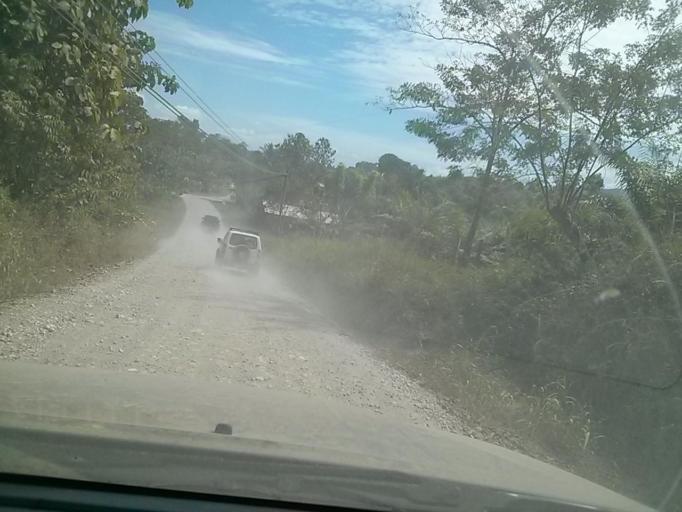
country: CR
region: Puntarenas
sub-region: Canton de Golfito
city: Golfito
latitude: 8.4542
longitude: -83.0498
